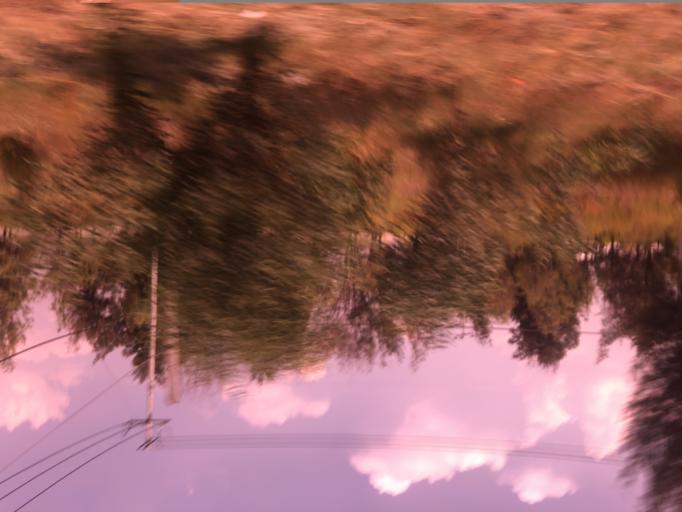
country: MX
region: Mexico
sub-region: Ciudad Nezahualcoyotl
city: Colonia Gustavo Baz Prada
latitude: 19.4721
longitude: -98.9974
